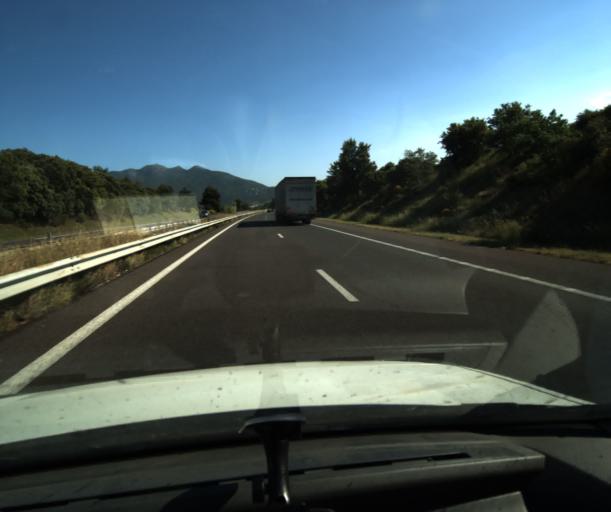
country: FR
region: Languedoc-Roussillon
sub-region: Departement des Pyrenees-Orientales
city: Banyuls-dels-Aspres
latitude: 42.5537
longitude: 2.8491
